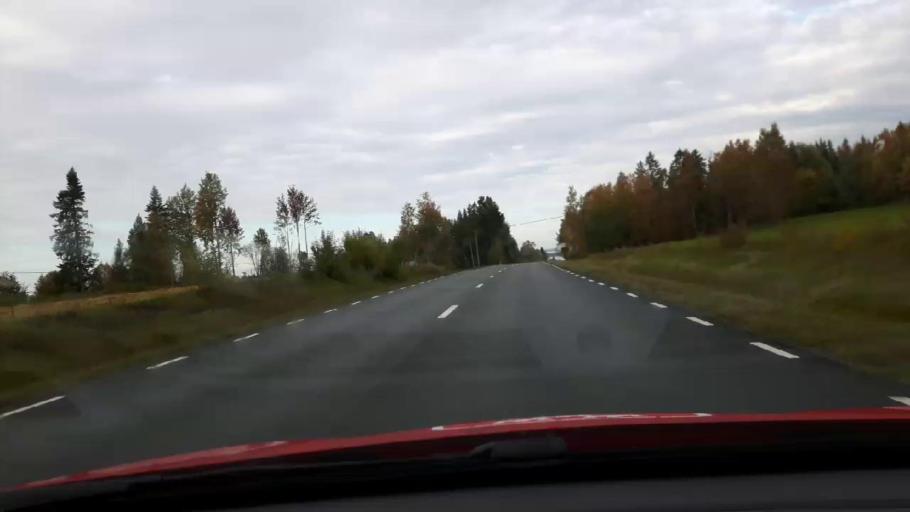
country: SE
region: Jaemtland
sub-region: Krokoms Kommun
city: Krokom
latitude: 63.1134
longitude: 14.2932
